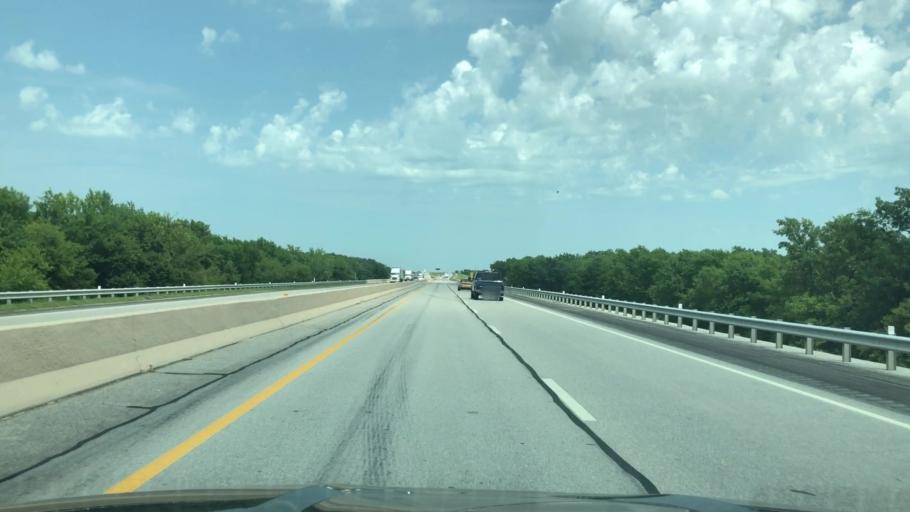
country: US
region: Oklahoma
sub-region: Rogers County
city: Catoosa
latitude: 36.1959
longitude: -95.7171
